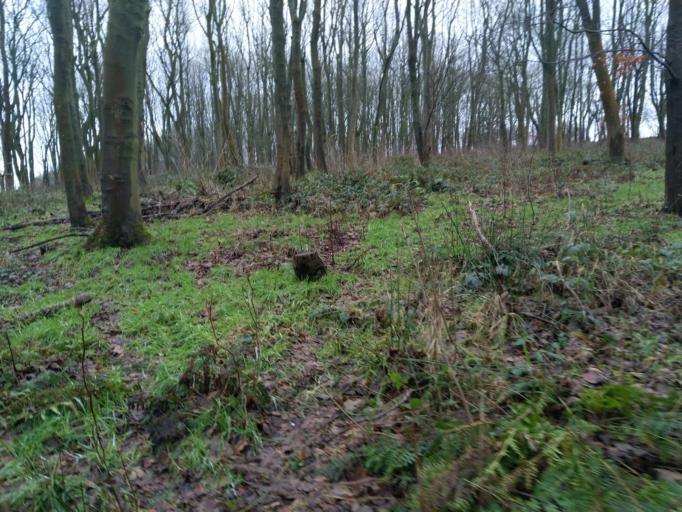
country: GB
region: Scotland
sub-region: Fife
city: Limekilns
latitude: 55.9922
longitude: -3.5164
